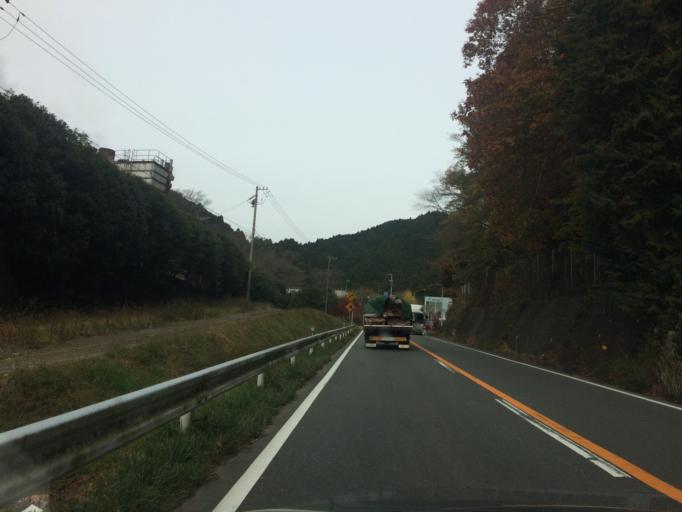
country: JP
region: Shizuoka
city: Fujinomiya
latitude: 35.1770
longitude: 138.5229
